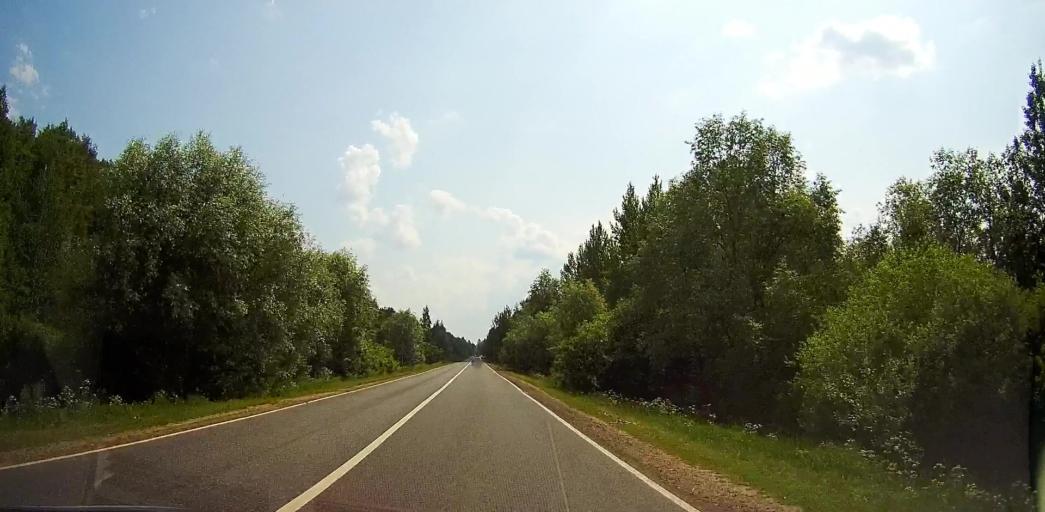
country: RU
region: Moskovskaya
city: Malino
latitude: 55.0938
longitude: 38.1648
